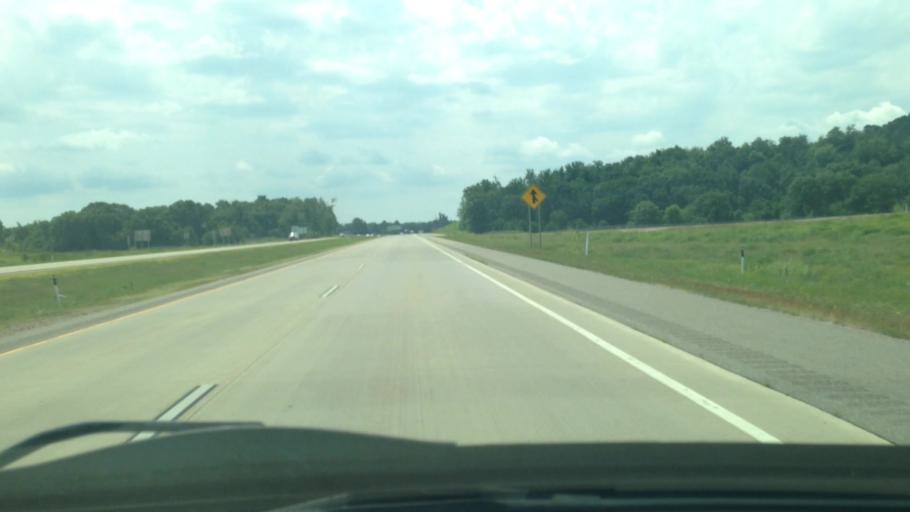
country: US
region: Wisconsin
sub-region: Sauk County
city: West Baraboo
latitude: 43.5138
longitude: -89.7841
